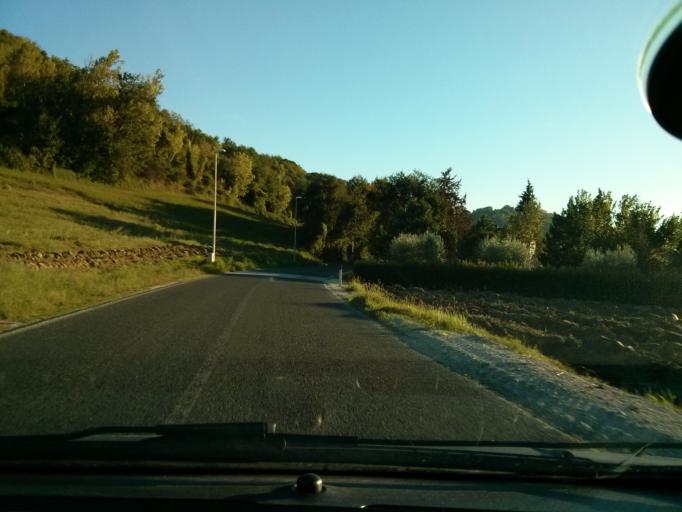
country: IT
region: The Marches
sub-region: Provincia di Pesaro e Urbino
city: Villanova
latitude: 43.7276
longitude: 12.9210
